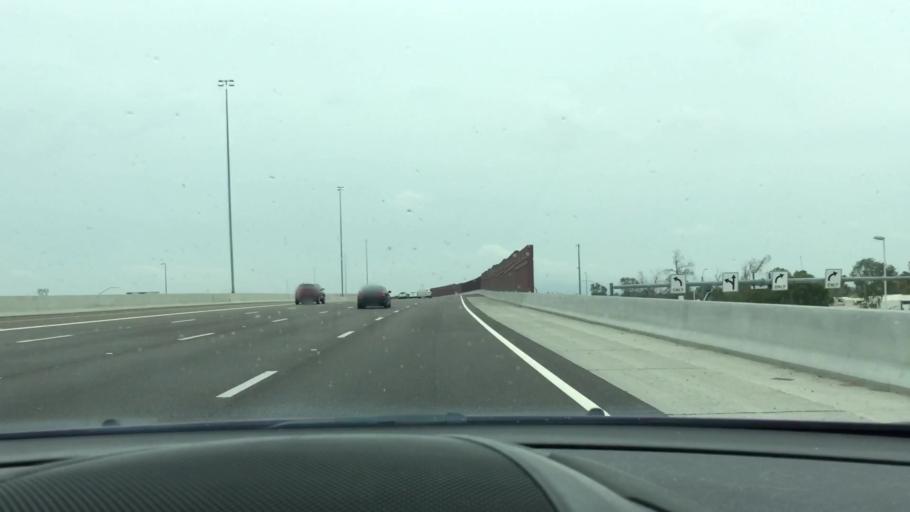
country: US
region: Arizona
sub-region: Maricopa County
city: Mesa
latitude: 33.4538
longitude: -111.8413
